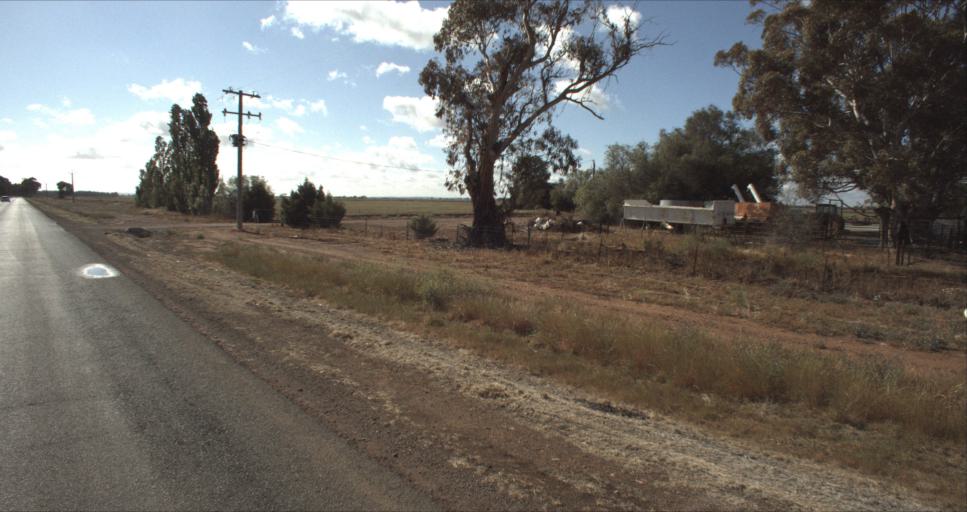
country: AU
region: New South Wales
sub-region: Leeton
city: Leeton
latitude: -34.5510
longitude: 146.3085
